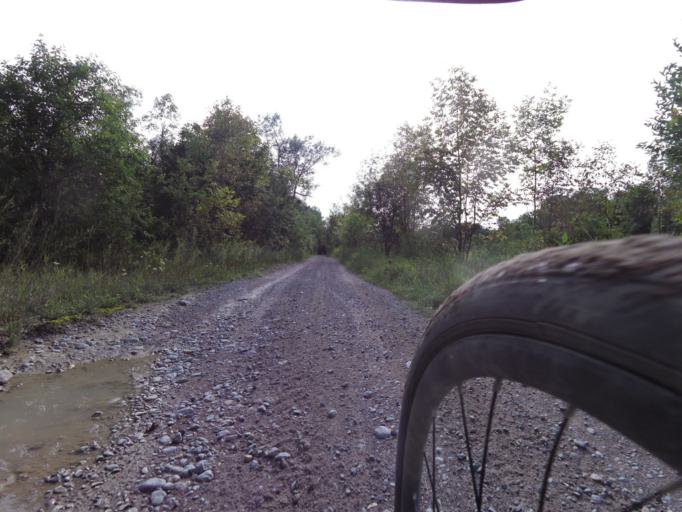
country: CA
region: Ontario
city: Quinte West
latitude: 44.0475
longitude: -77.6250
